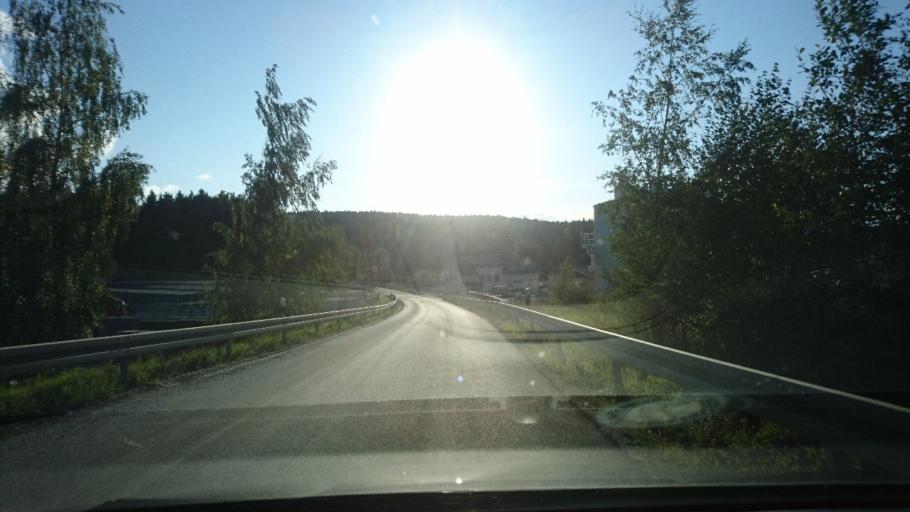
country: DE
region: Bavaria
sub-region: Upper Franconia
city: Berg
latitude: 50.3637
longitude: 11.7607
